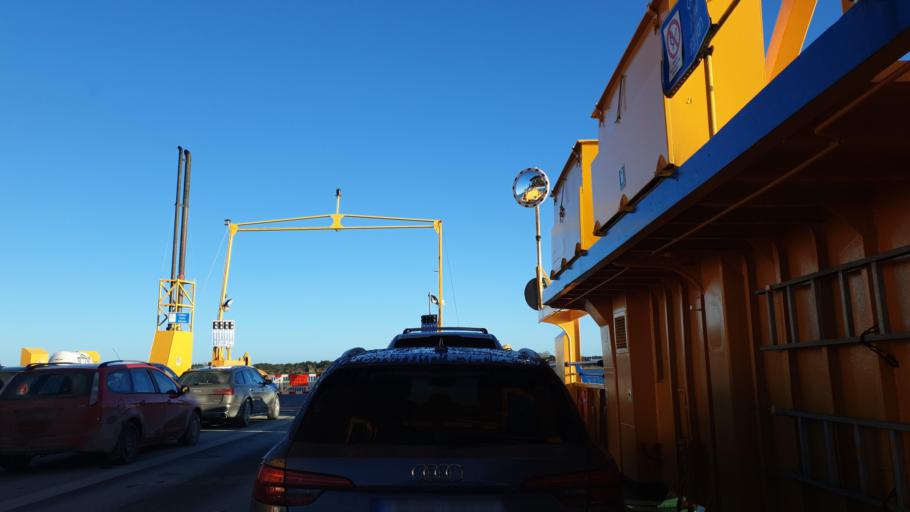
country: SE
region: Gotland
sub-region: Gotland
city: Slite
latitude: 57.8670
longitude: 19.0728
